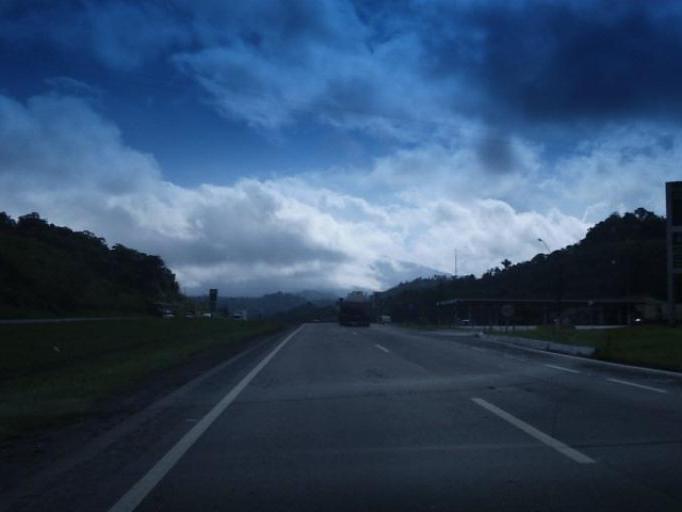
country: BR
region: Parana
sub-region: Antonina
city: Antonina
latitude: -25.1085
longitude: -48.7447
